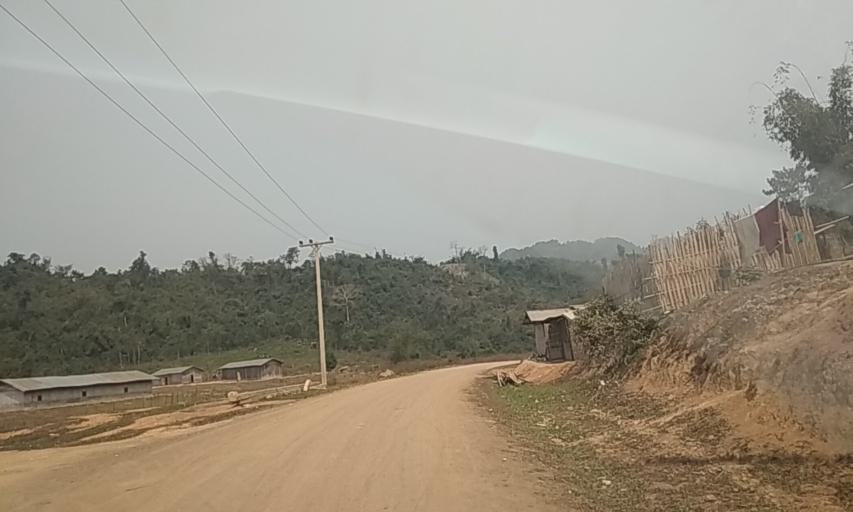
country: VN
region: Huyen Dien Bien
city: Dien Bien Phu
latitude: 21.4253
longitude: 102.7624
